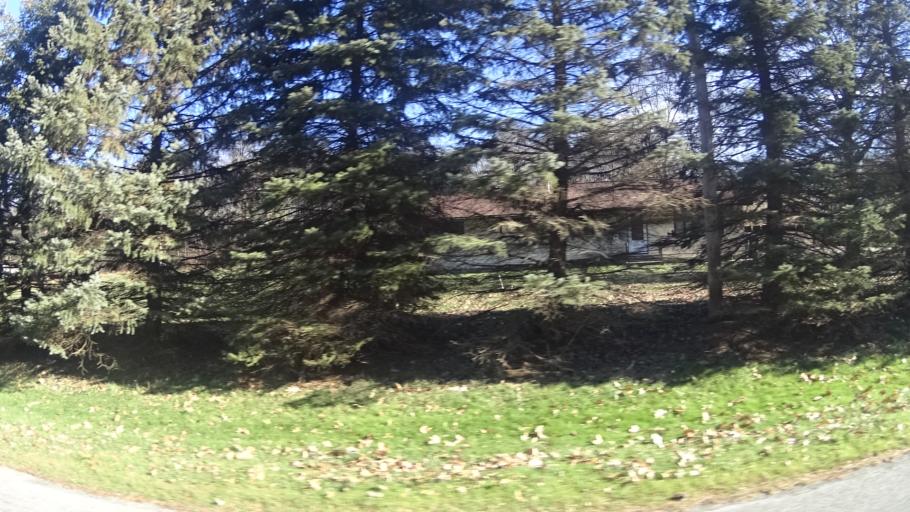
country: US
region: Ohio
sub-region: Lorain County
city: South Amherst
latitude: 41.3523
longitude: -82.2913
